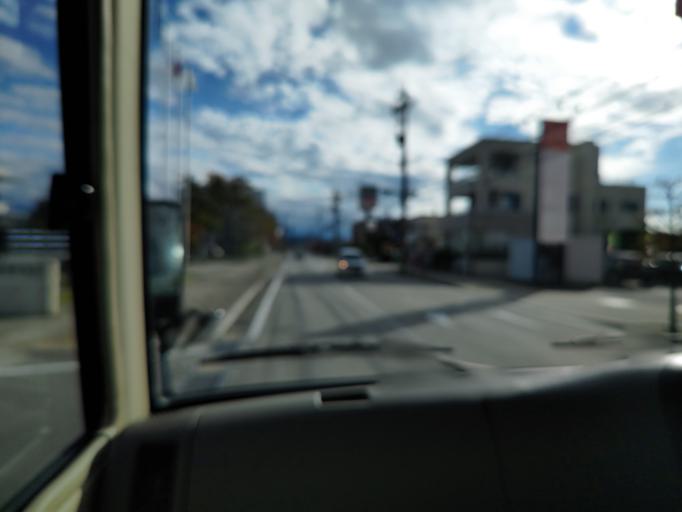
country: JP
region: Toyama
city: Nyuzen
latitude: 36.8712
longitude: 137.4471
